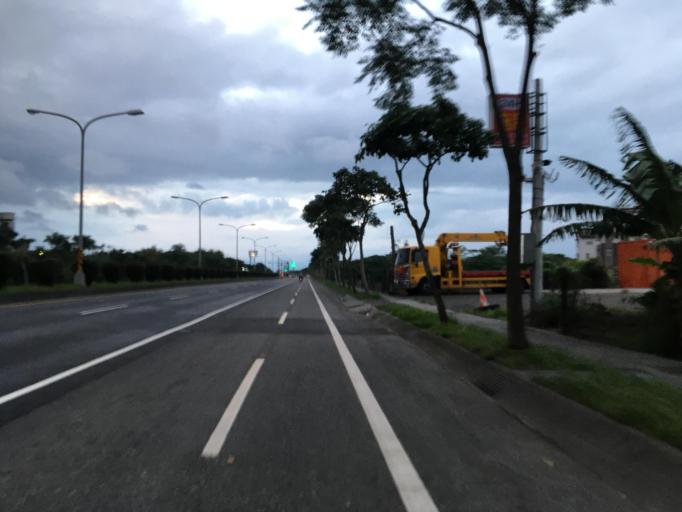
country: TW
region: Taiwan
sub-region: Yilan
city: Yilan
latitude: 24.6138
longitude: 121.8508
